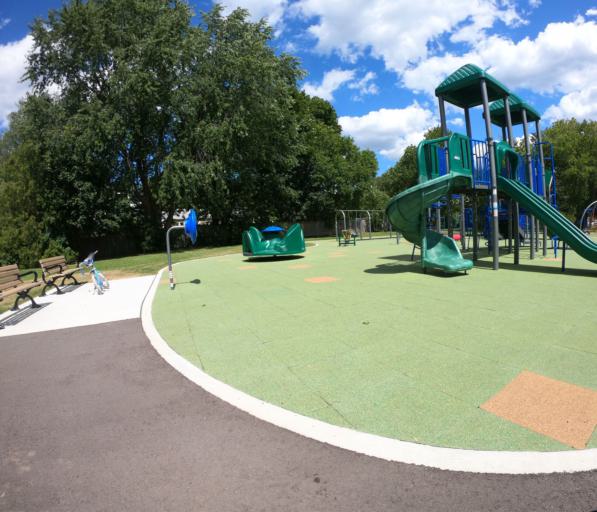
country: CA
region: Ontario
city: Etobicoke
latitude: 43.6338
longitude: -79.5451
